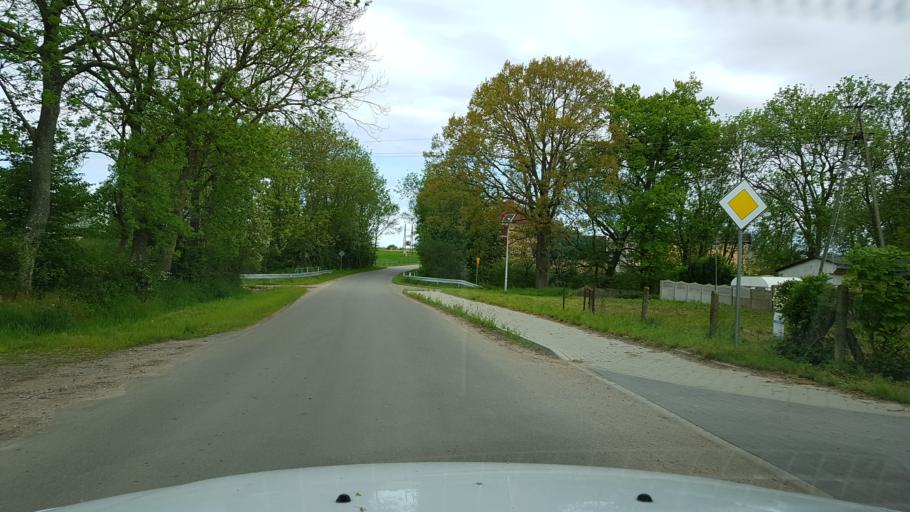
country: PL
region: West Pomeranian Voivodeship
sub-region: Powiat kolobrzeski
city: Ustronie Morskie
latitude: 54.2119
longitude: 15.8226
